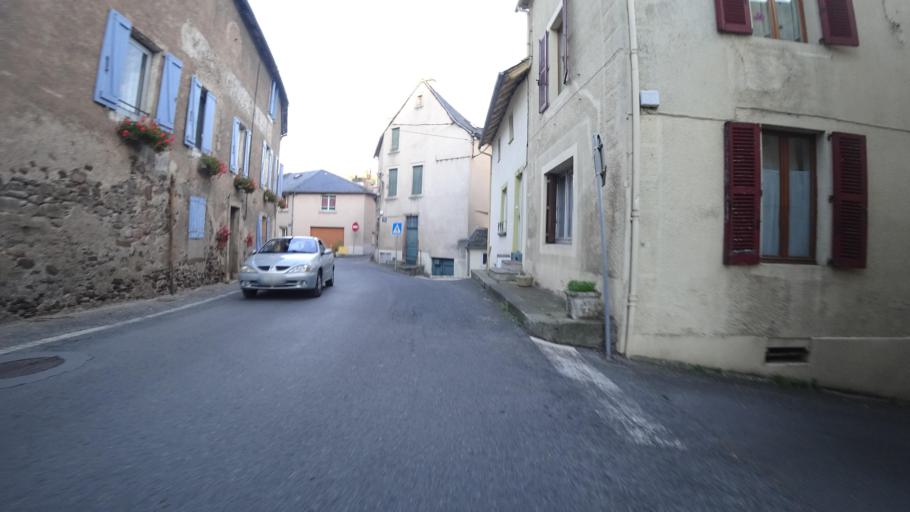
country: FR
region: Midi-Pyrenees
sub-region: Departement de l'Aveyron
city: Le Monastere
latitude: 44.3425
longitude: 2.5787
